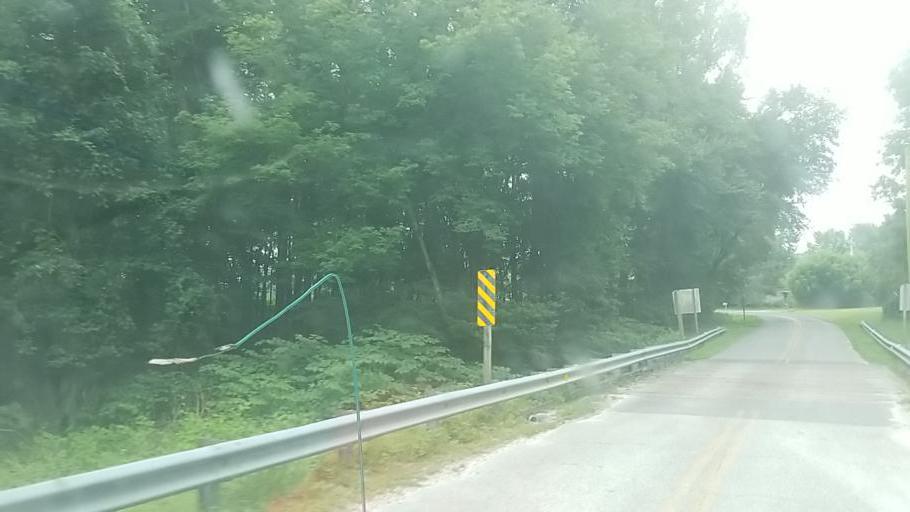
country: US
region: Delaware
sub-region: Sussex County
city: Selbyville
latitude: 38.4462
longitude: -75.2114
